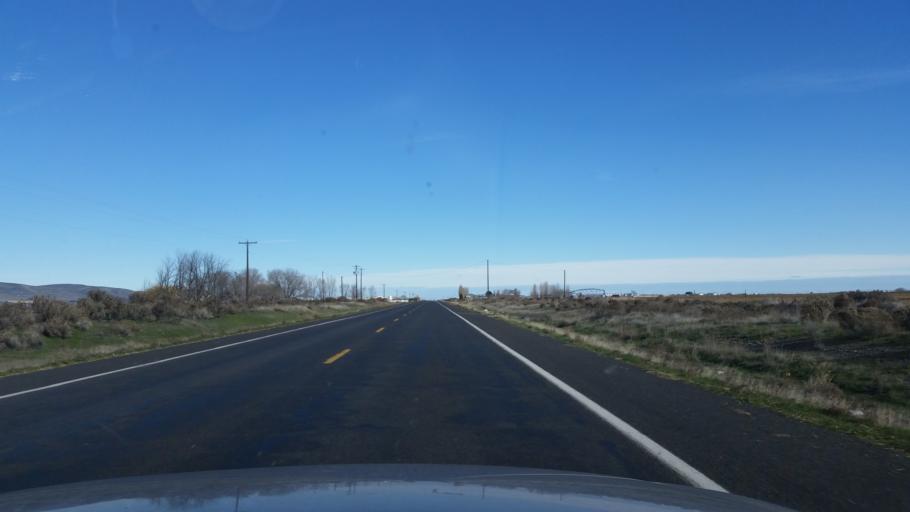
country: US
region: Washington
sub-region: Grant County
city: Ephrata
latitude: 47.2134
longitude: -119.6555
